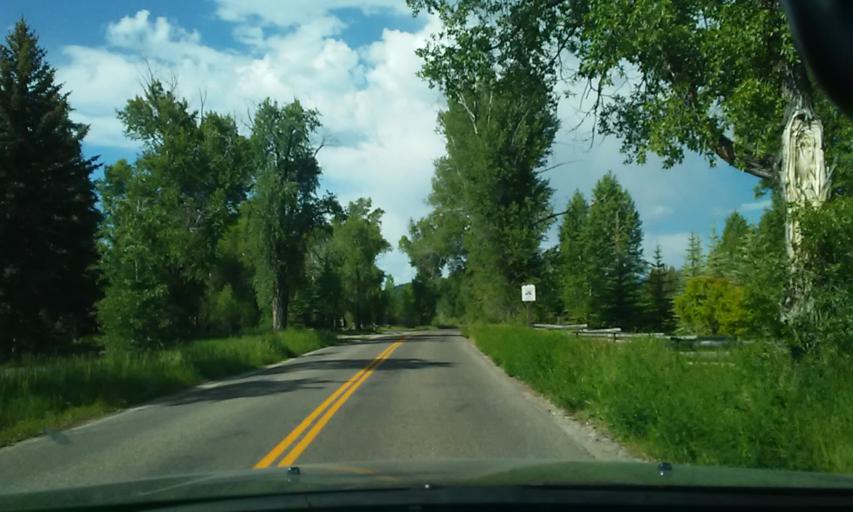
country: US
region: Wyoming
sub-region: Teton County
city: Jackson
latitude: 43.5649
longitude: -110.7483
